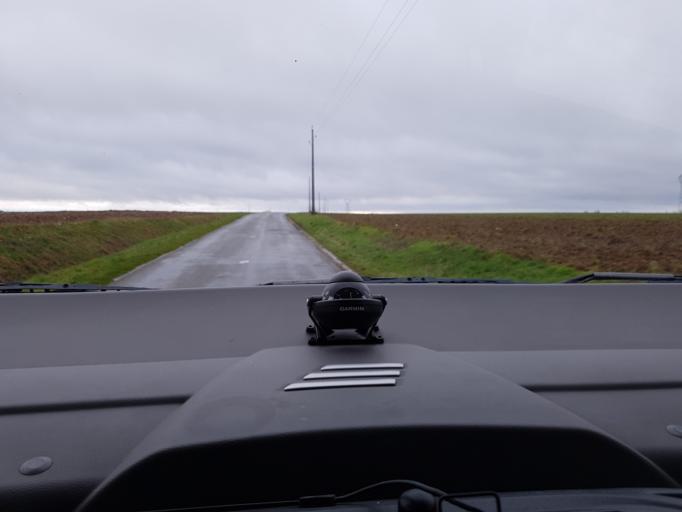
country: FR
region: Haute-Normandie
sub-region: Departement de l'Eure
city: Pont-Saint-Pierre
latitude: 49.3012
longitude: 1.3267
